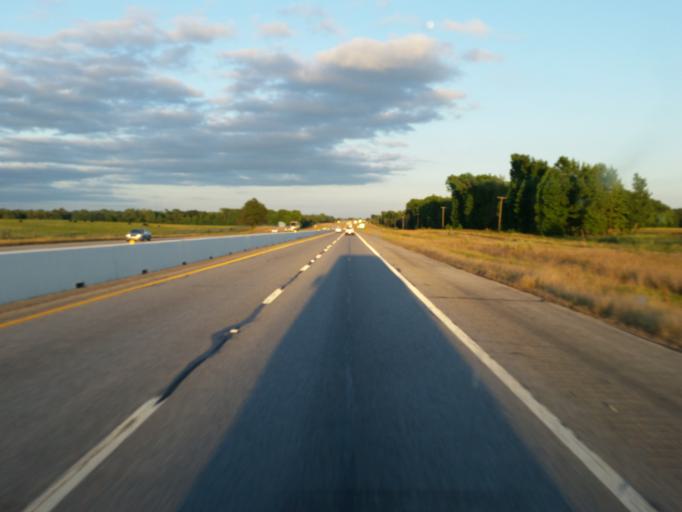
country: US
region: Texas
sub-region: Van Zandt County
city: Van
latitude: 32.5373
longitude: -95.7429
